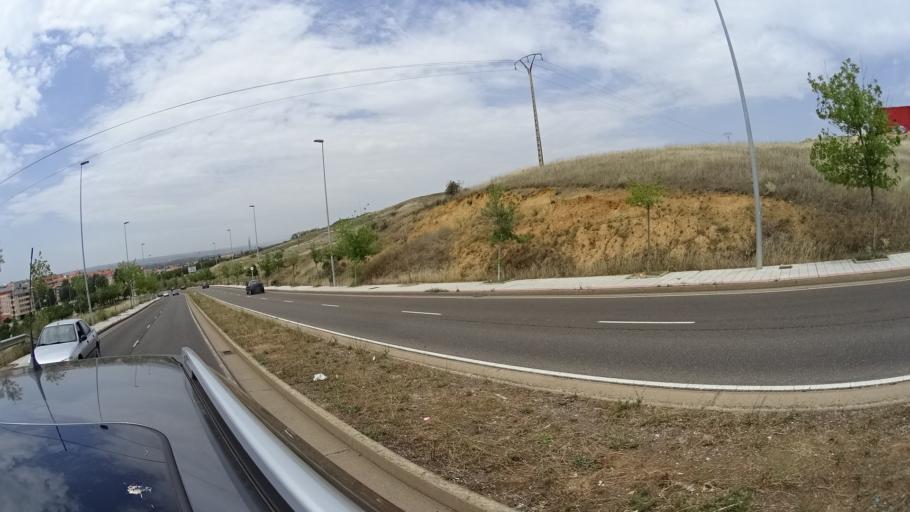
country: ES
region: Castille and Leon
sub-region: Provincia de Leon
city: Leon
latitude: 42.6120
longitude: -5.5818
